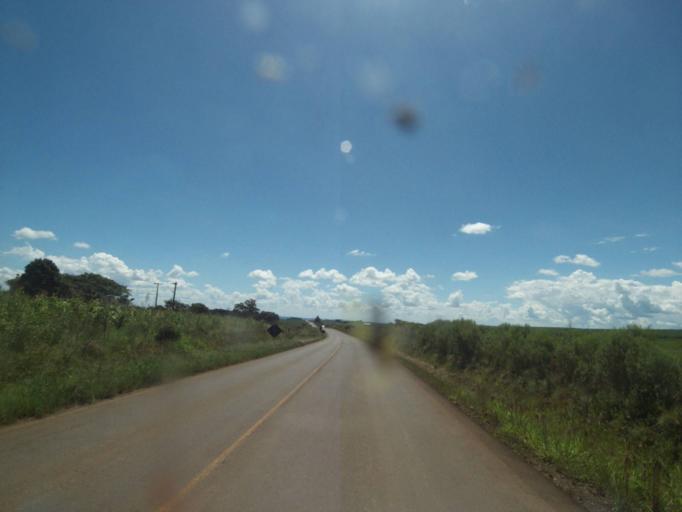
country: BR
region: Parana
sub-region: Pinhao
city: Pinhao
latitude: -25.8135
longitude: -52.0455
